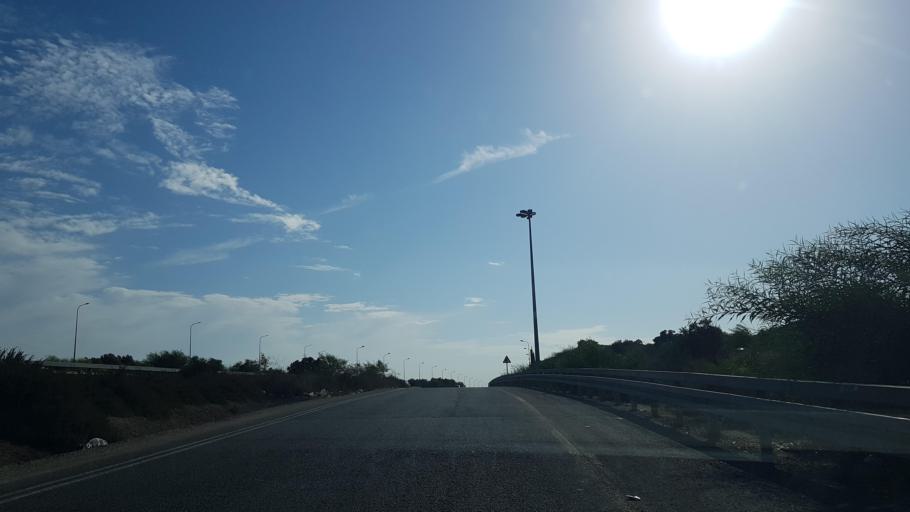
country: IL
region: Northern District
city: Timrat
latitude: 32.7339
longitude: 35.2105
